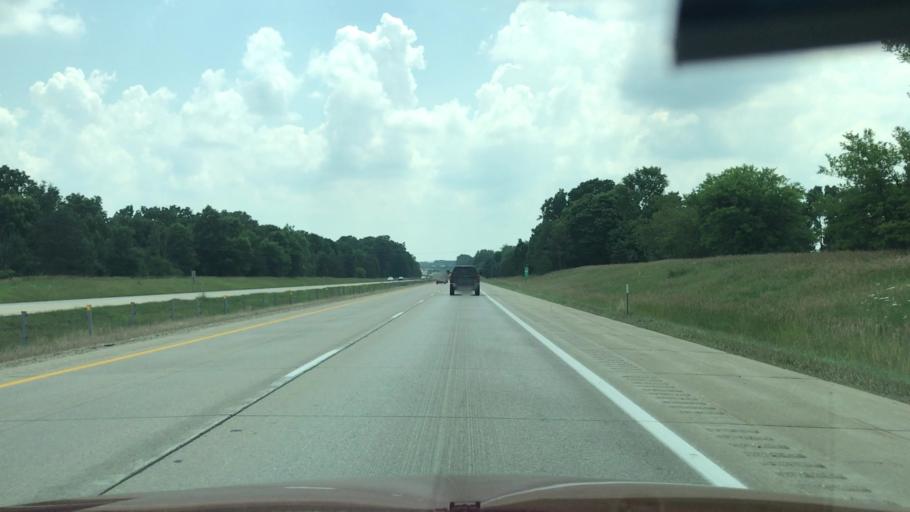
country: US
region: Michigan
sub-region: Allegan County
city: Plainwell
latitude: 42.4808
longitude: -85.6526
